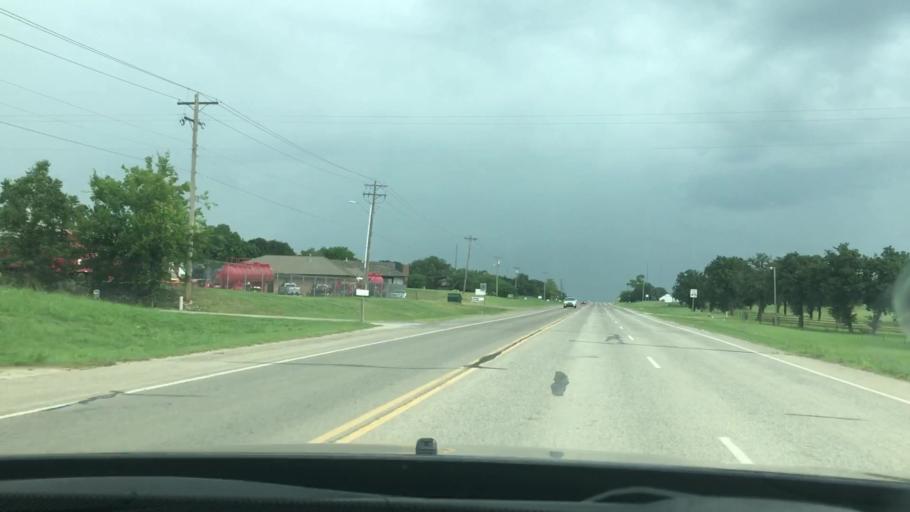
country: US
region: Oklahoma
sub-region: Carter County
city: Healdton
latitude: 34.2125
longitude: -97.4748
